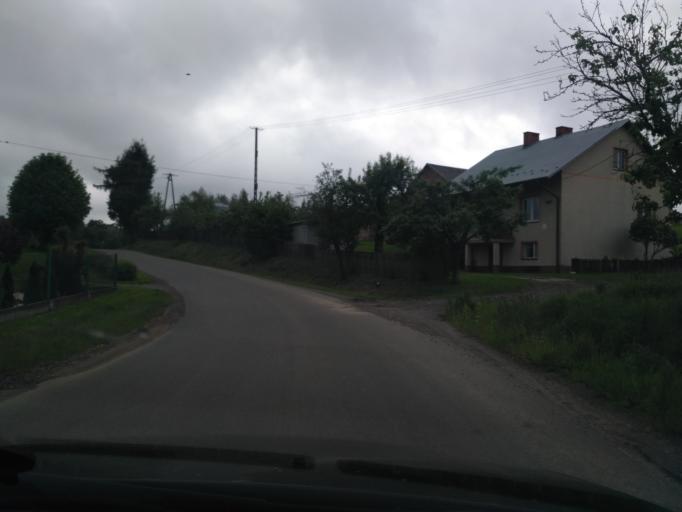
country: PL
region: Subcarpathian Voivodeship
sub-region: Powiat strzyzowski
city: Frysztak
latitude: 49.8042
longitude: 21.5616
